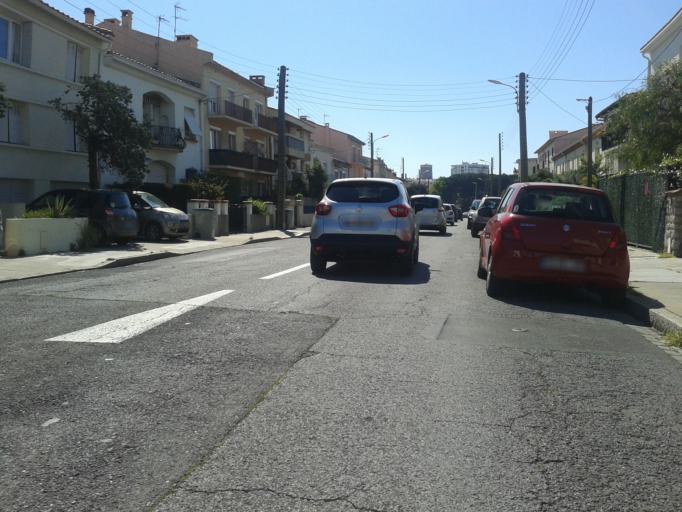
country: FR
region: Languedoc-Roussillon
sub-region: Departement des Pyrenees-Orientales
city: Perpignan
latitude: 42.6892
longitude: 2.8997
